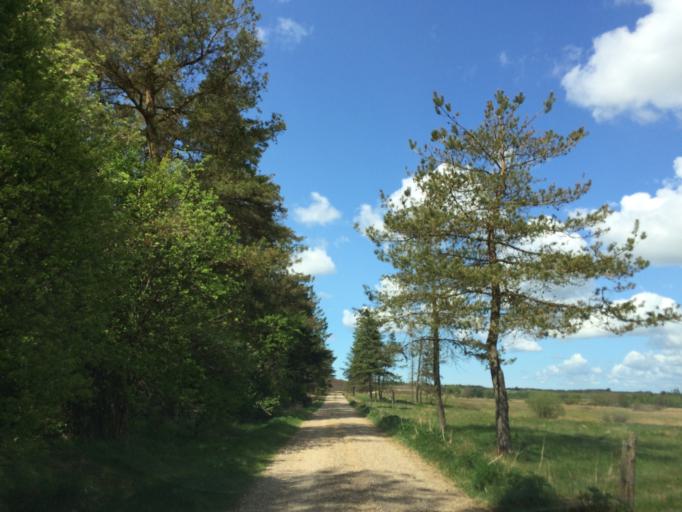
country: DK
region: Central Jutland
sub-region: Holstebro Kommune
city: Ulfborg
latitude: 56.2795
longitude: 8.4655
